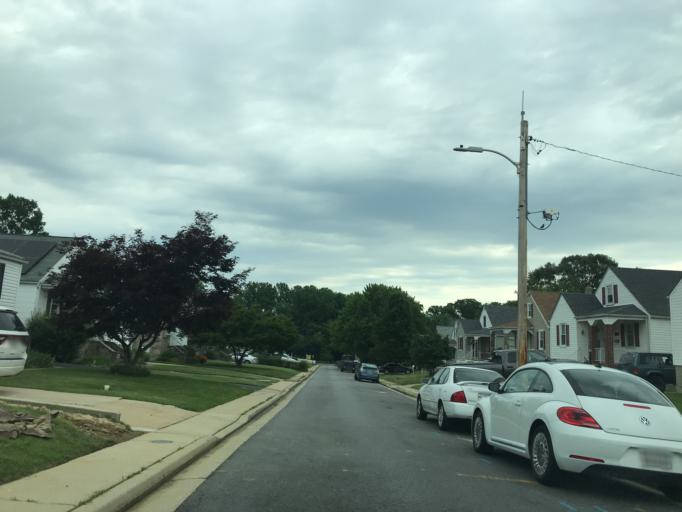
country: US
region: Maryland
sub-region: Baltimore County
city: Overlea
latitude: 39.3561
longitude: -76.5129
